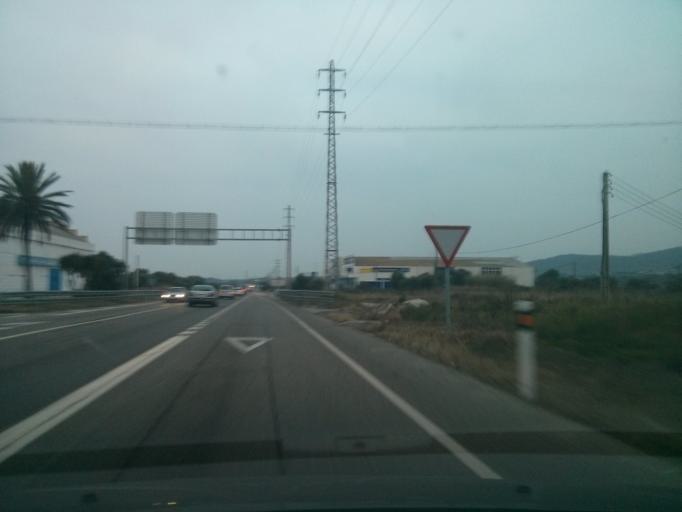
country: ES
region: Catalonia
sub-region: Provincia de Tarragona
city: El Vendrell
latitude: 41.2056
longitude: 1.5315
